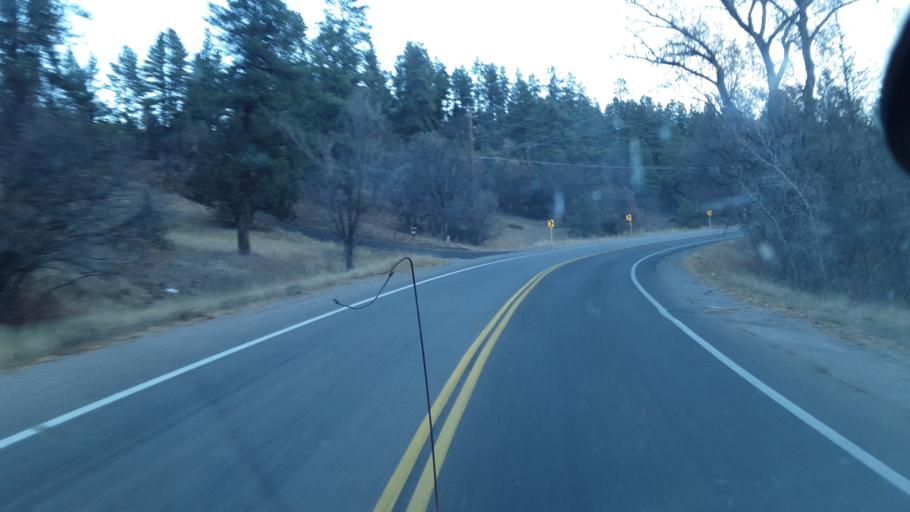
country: US
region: Colorado
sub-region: La Plata County
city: Durango
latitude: 37.3053
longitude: -107.8310
